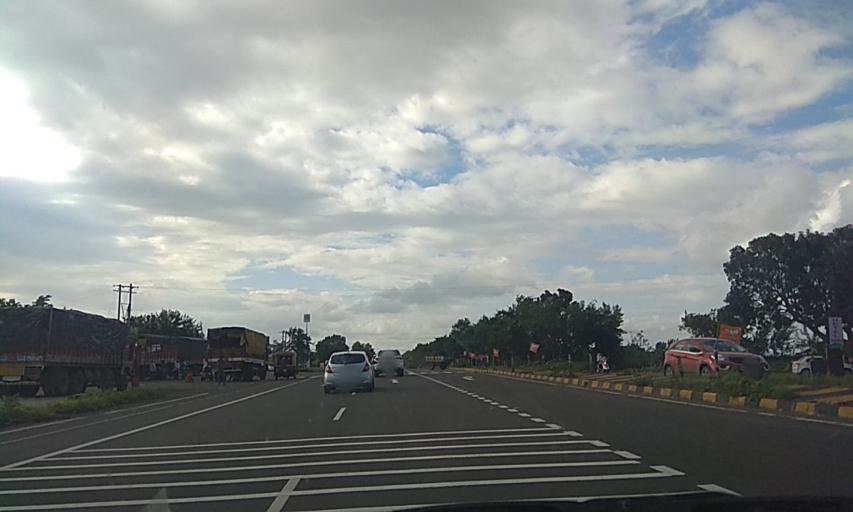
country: IN
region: Maharashtra
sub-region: Satara Division
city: Karad
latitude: 17.1155
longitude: 74.1981
